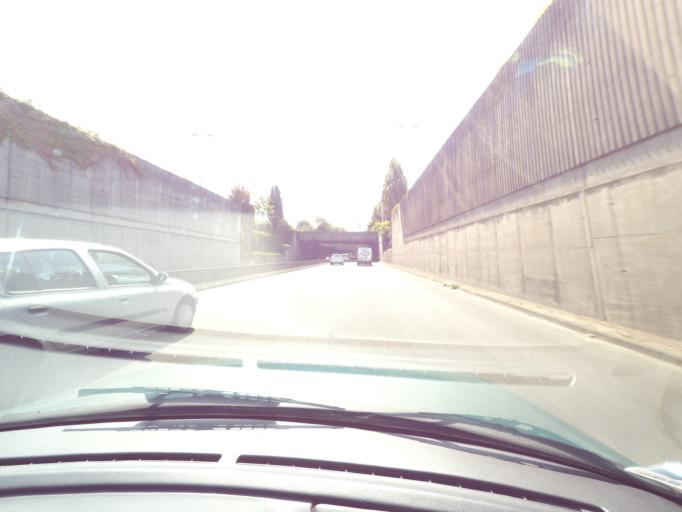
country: FR
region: Limousin
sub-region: Departement de la Haute-Vienne
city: Limoges
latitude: 45.8277
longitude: 1.2832
